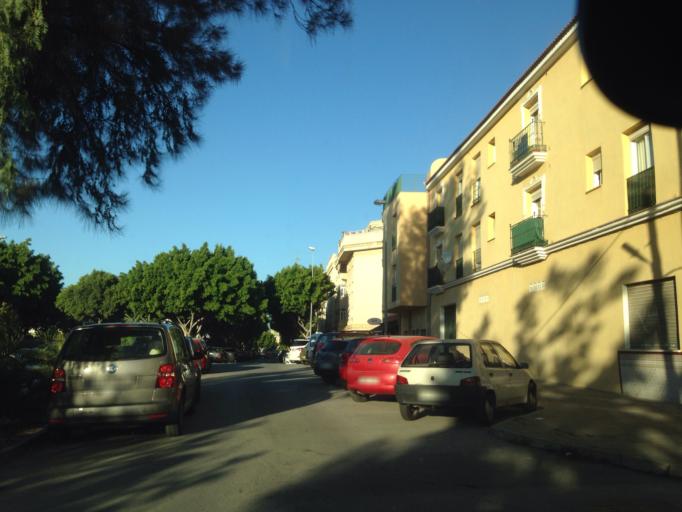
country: ES
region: Andalusia
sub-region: Provincia de Malaga
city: Malaga
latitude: 36.7208
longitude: -4.4723
